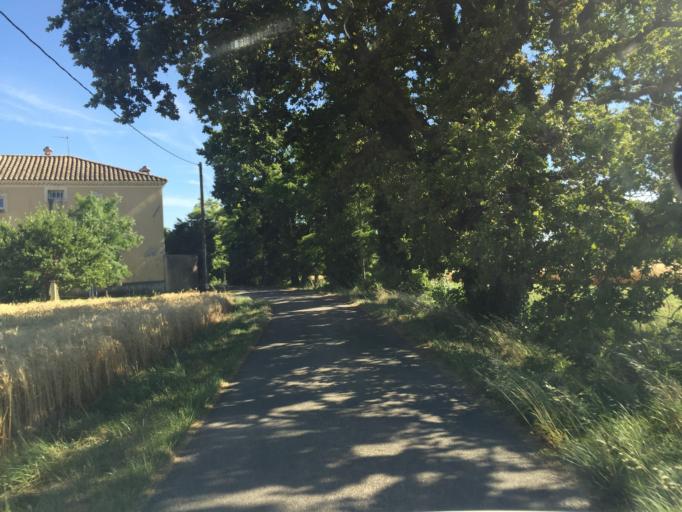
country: FR
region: Provence-Alpes-Cote d'Azur
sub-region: Departement du Vaucluse
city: Caderousse
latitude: 44.1067
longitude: 4.7418
